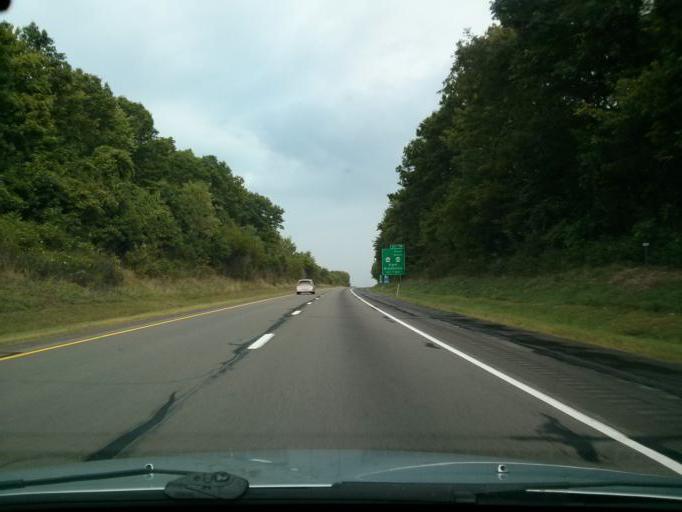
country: US
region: Pennsylvania
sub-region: Jefferson County
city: Brookville
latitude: 41.1766
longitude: -79.1198
